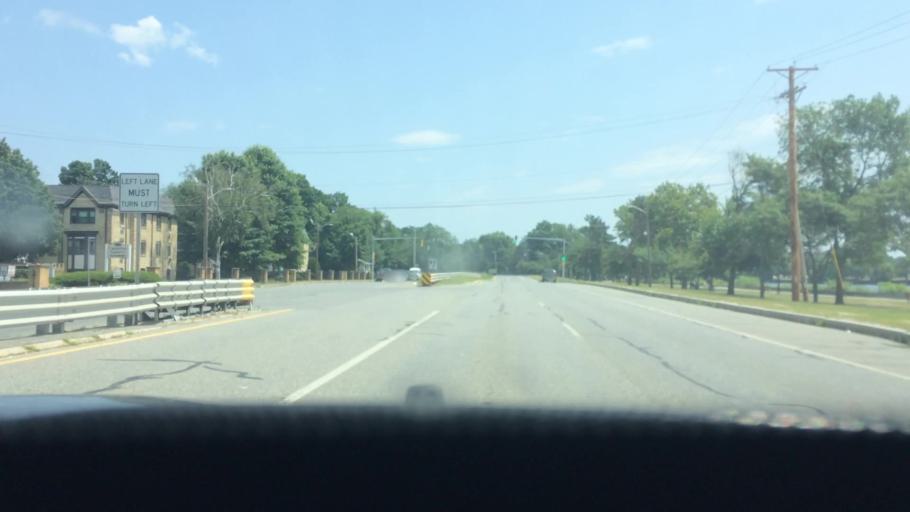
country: US
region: Massachusetts
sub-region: Middlesex County
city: Lowell
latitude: 42.6415
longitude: -71.3462
